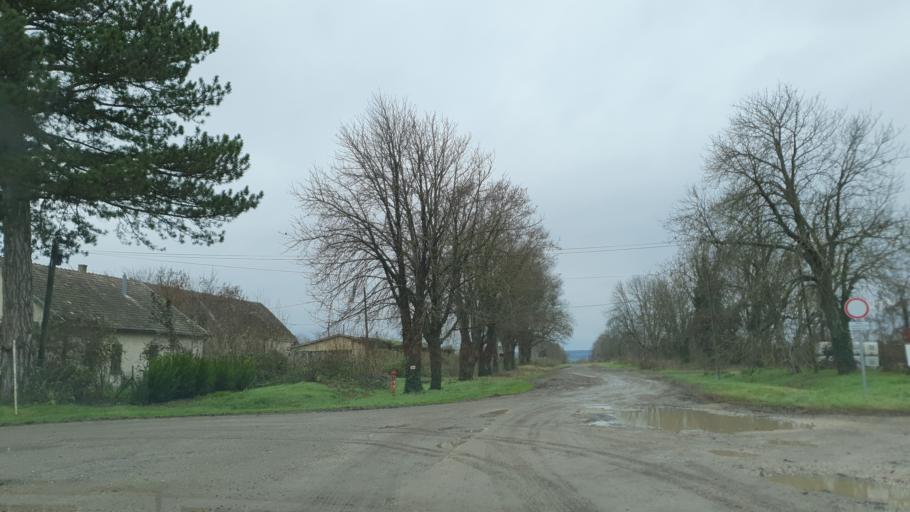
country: HU
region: Zala
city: Keszthely
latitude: 46.7492
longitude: 17.2270
